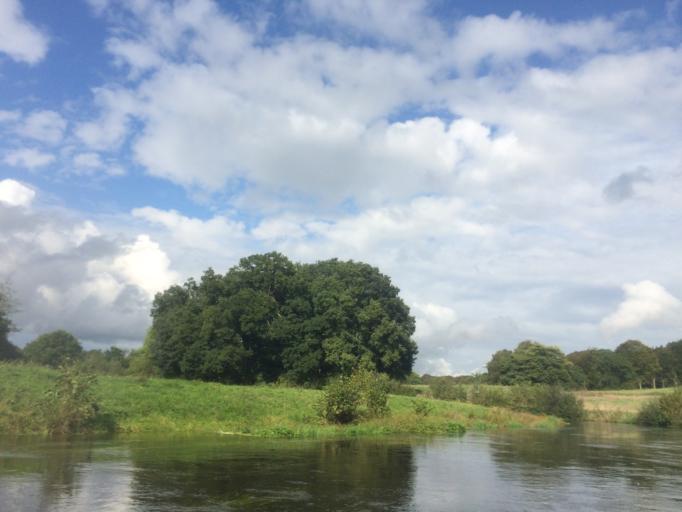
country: DK
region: South Denmark
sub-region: Vejle Kommune
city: Egtved
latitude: 55.6516
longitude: 9.3097
